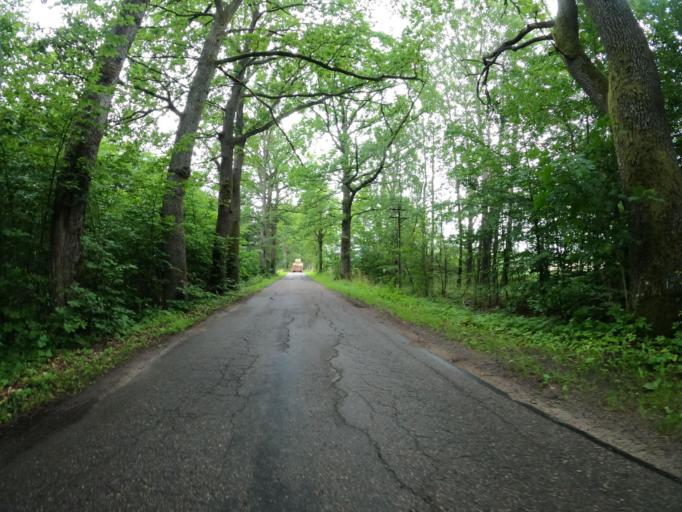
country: PL
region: West Pomeranian Voivodeship
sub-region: Powiat koszalinski
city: Bobolice
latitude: 53.9098
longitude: 16.5079
